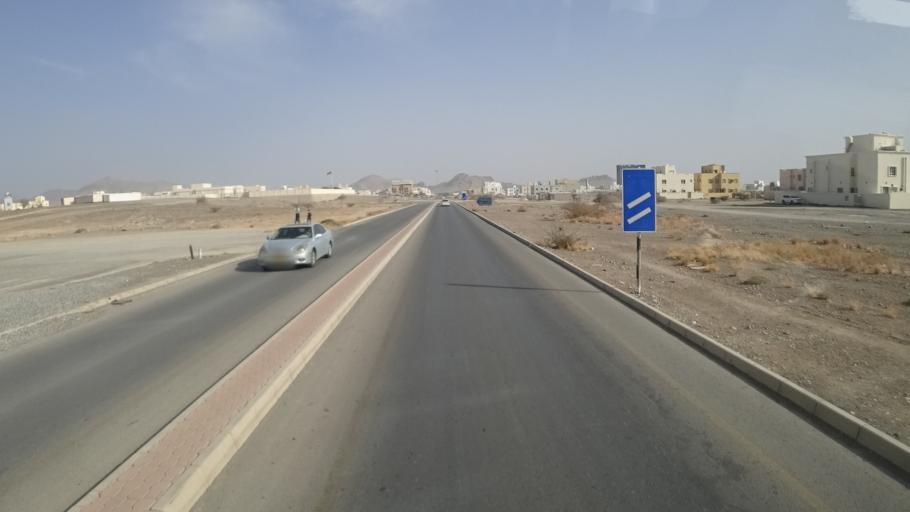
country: OM
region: Muhafazat ad Dakhiliyah
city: Nizwa
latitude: 22.8747
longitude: 57.5409
